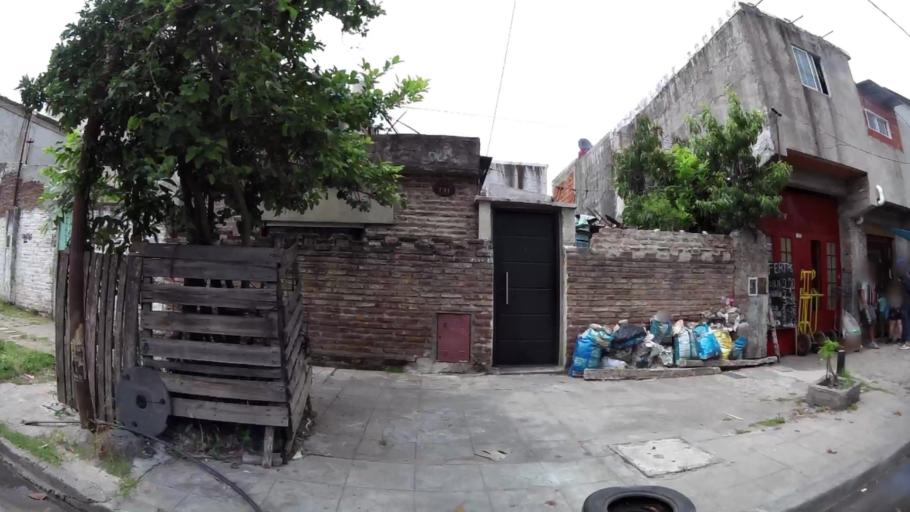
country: AR
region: Buenos Aires
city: San Justo
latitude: -34.6698
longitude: -58.5183
